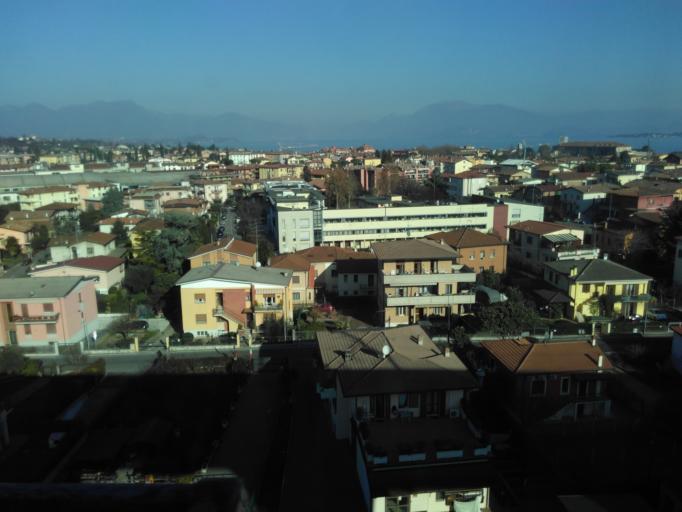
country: IT
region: Lombardy
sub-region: Provincia di Brescia
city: Desenzano del Garda
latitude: 45.4655
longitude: 10.5299
